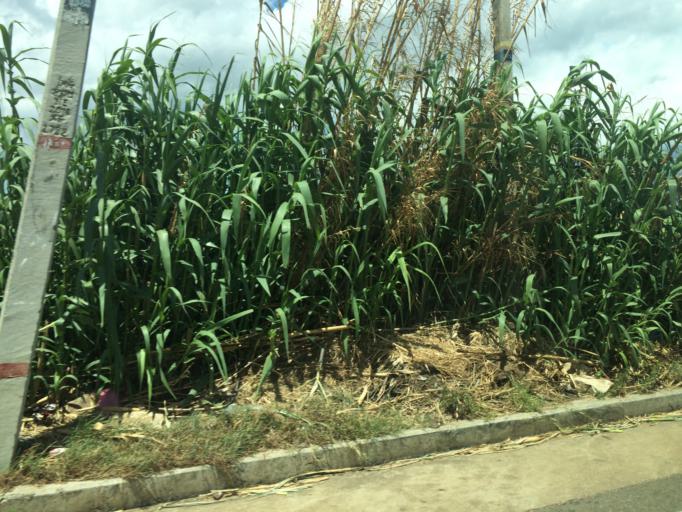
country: LK
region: Central
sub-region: Nuwara Eliya District
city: Nuwara Eliya
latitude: 6.9067
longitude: 80.8434
